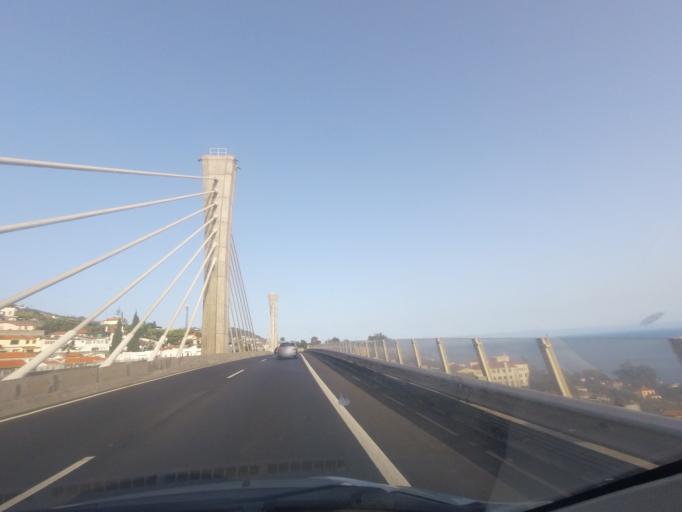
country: PT
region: Madeira
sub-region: Funchal
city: Nossa Senhora do Monte
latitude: 32.6623
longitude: -16.9077
